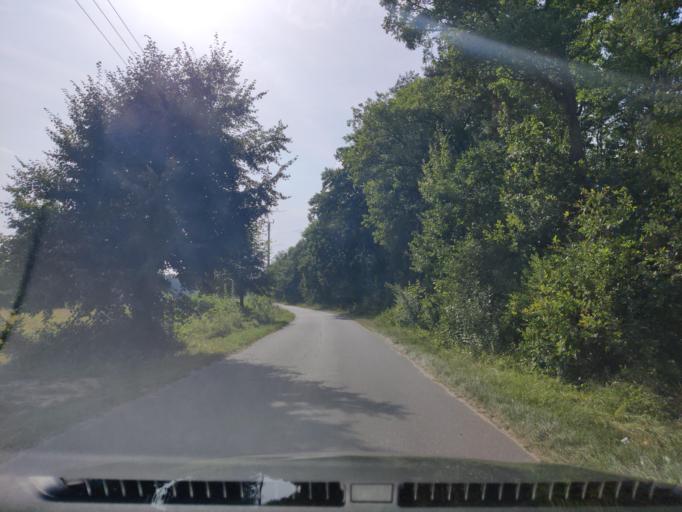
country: PL
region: Masovian Voivodeship
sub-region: Powiat pultuski
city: Obryte
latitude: 52.7671
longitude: 21.2355
